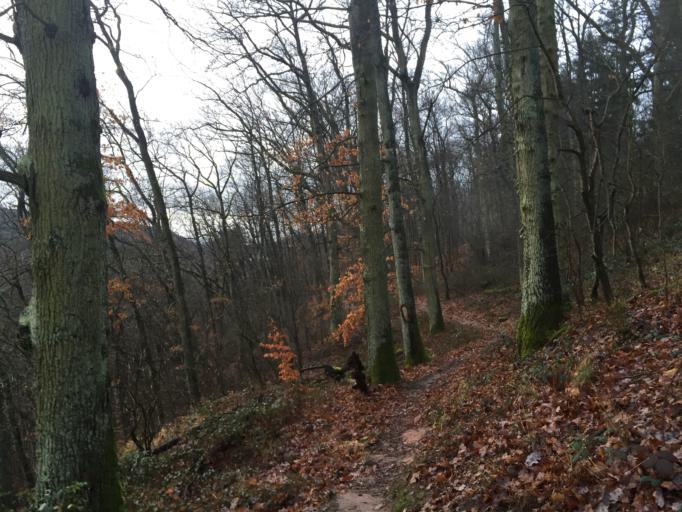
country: DE
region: Rheinland-Pfalz
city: Tiefenthal
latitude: 49.5343
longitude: 8.1123
